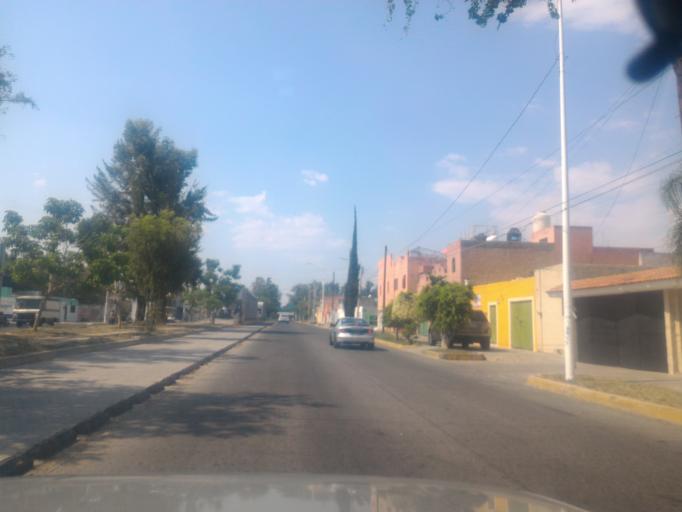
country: MX
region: Jalisco
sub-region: Zapopan
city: San Isidro
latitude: 20.7363
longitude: -103.3123
